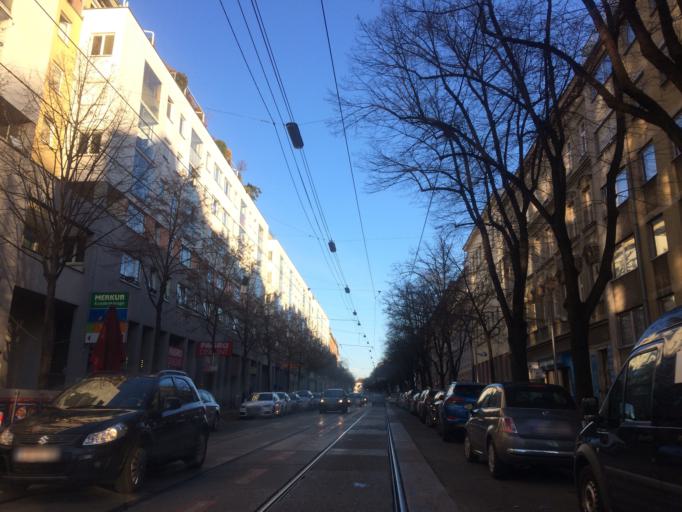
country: AT
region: Vienna
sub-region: Wien Stadt
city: Vienna
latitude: 48.1975
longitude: 16.2976
